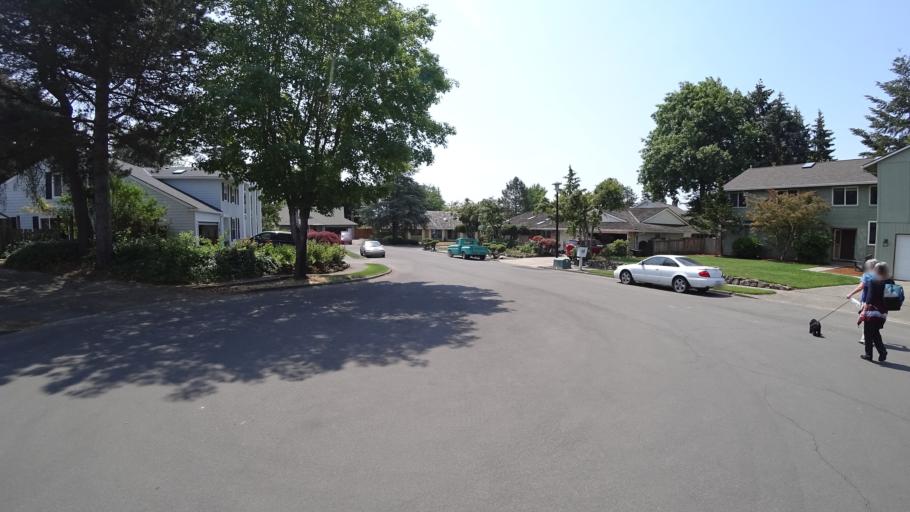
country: US
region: Oregon
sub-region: Washington County
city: Oak Hills
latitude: 45.5382
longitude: -122.8374
